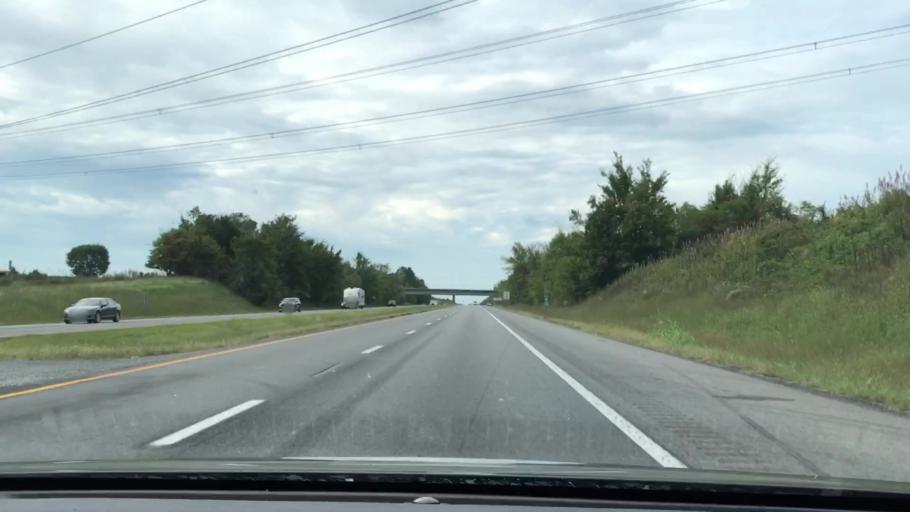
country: US
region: Kentucky
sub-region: Marshall County
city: Calvert City
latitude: 36.9719
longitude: -88.3467
